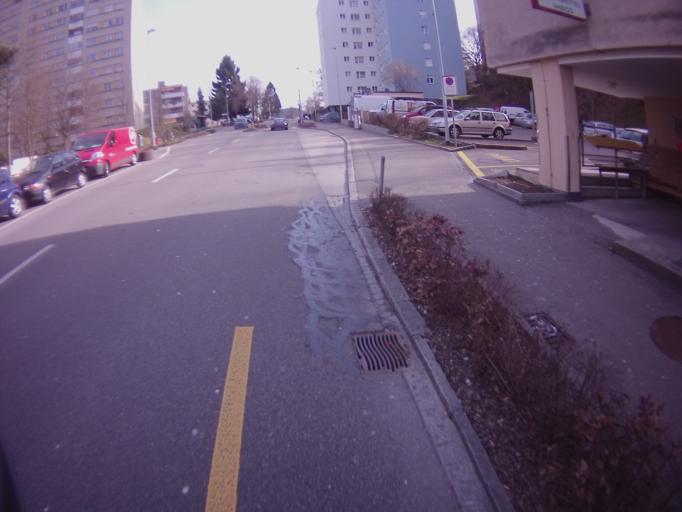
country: CH
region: Aargau
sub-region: Bezirk Baden
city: Spreitenbach
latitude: 47.4236
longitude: 8.3627
